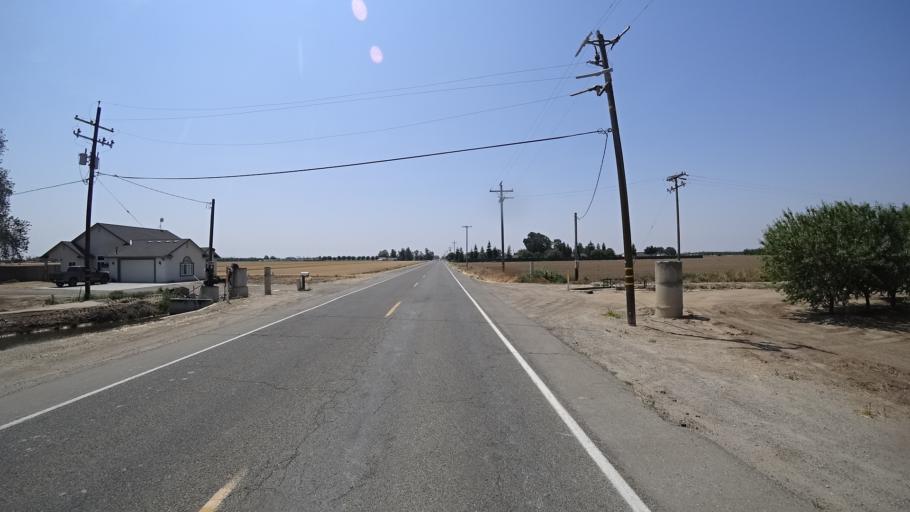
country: US
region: California
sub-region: Kings County
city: Lemoore
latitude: 36.3355
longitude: -119.7808
